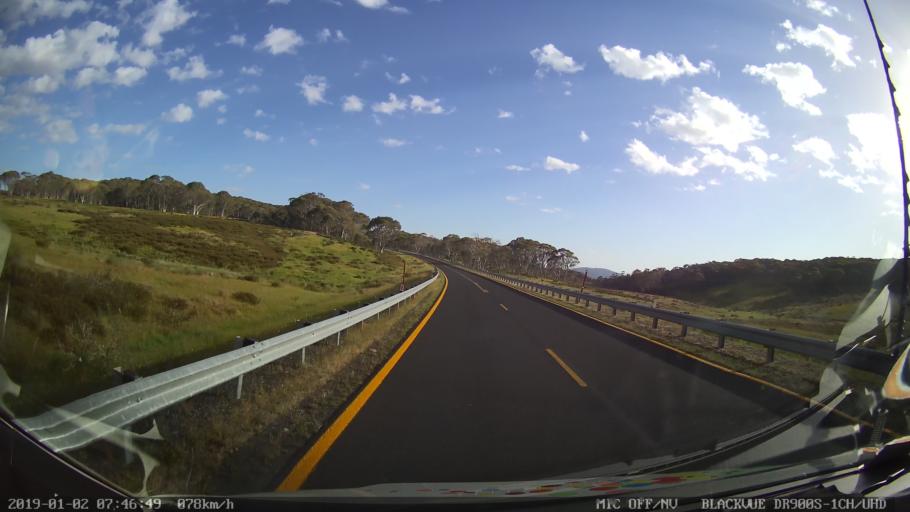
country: AU
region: New South Wales
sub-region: Tumut Shire
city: Tumut
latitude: -35.7716
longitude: 148.5203
